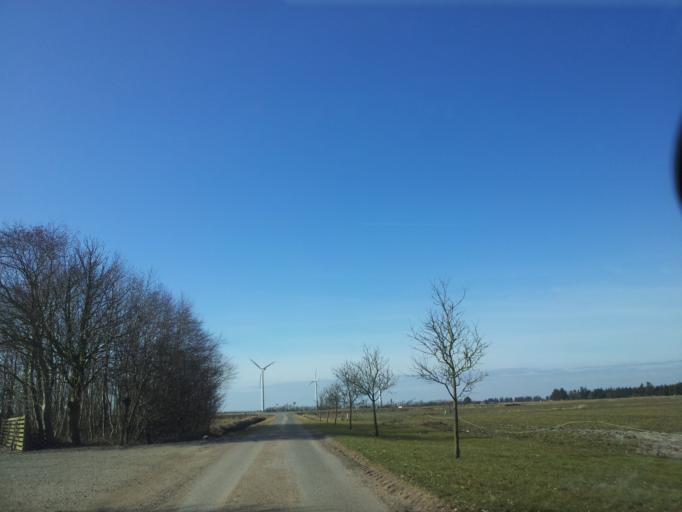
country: DK
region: South Denmark
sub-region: Tonder Kommune
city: Sherrebek
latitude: 55.2100
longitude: 8.7285
